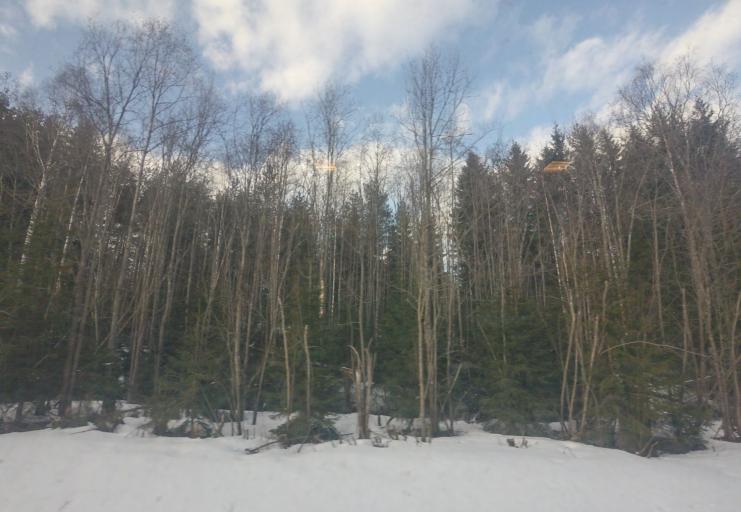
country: FI
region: Southern Savonia
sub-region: Savonlinna
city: Kerimaeki
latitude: 61.8638
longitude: 29.1045
